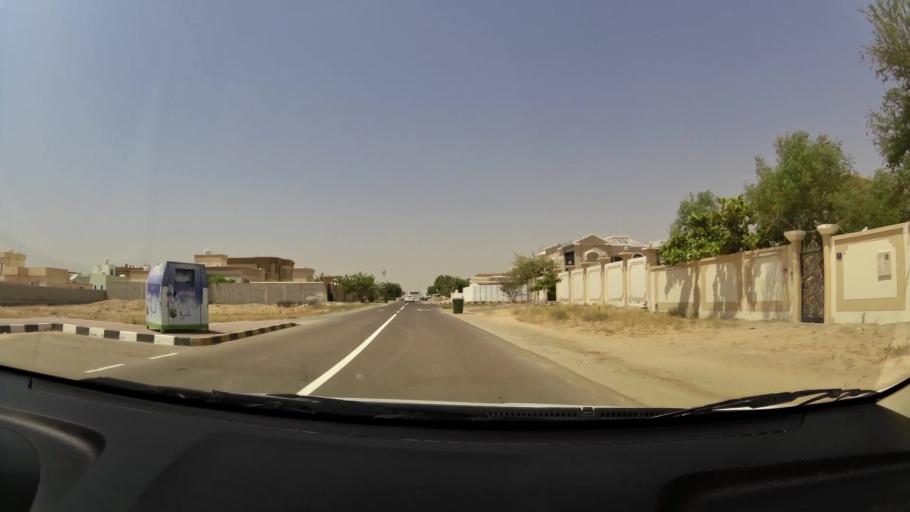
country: AE
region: Ajman
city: Ajman
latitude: 25.4252
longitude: 55.5179
